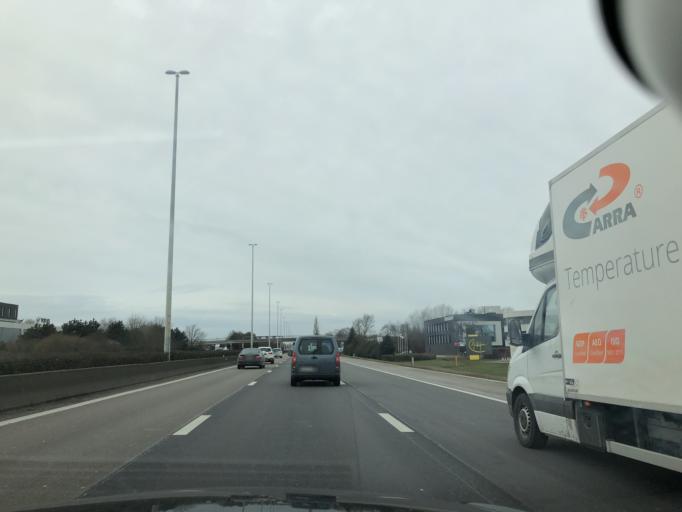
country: BE
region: Flanders
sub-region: Provincie Antwerpen
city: Wommelgem
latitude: 51.2118
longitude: 4.5179
